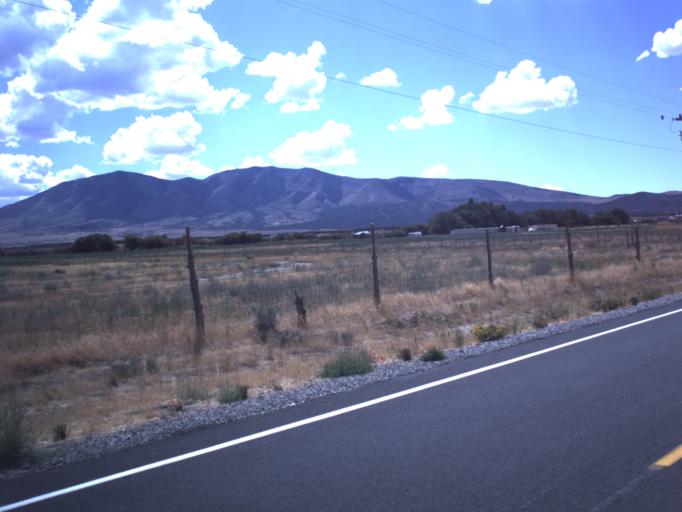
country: US
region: Utah
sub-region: Tooele County
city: Tooele
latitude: 40.3366
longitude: -112.4512
